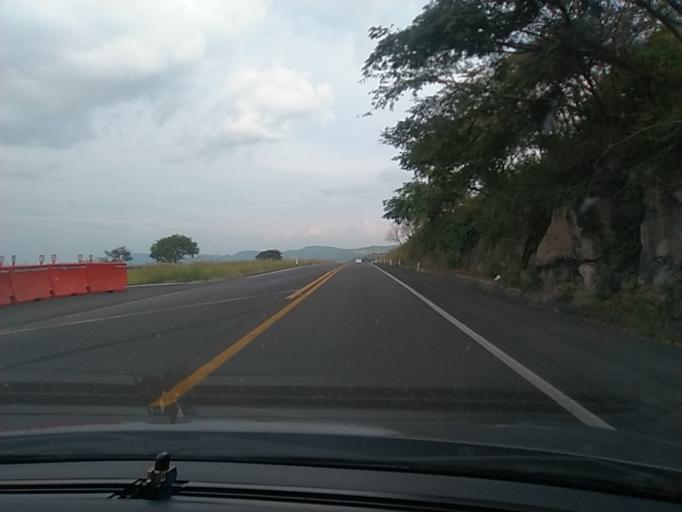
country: MX
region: Michoacan
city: Copandaro de Galeana
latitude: 19.8972
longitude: -101.2559
